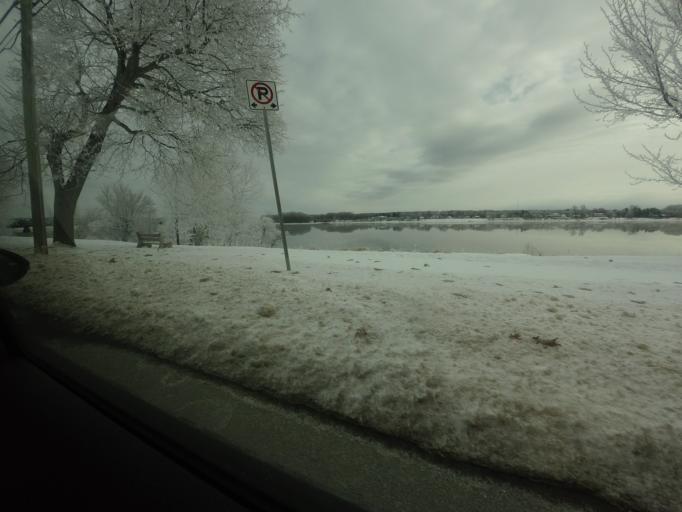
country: CA
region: New Brunswick
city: Fredericton
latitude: 45.9519
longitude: -66.6327
